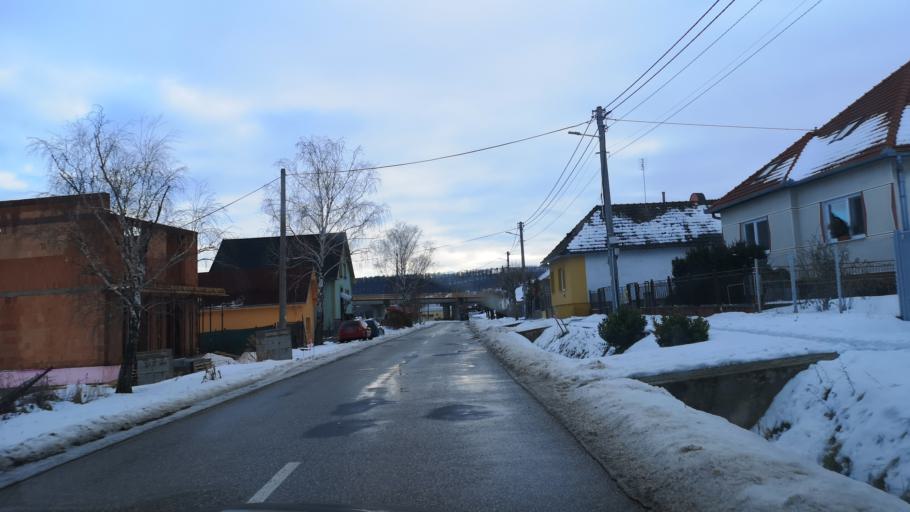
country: SK
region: Nitriansky
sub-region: Okres Nitra
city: Vrable
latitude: 48.1076
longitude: 18.3373
